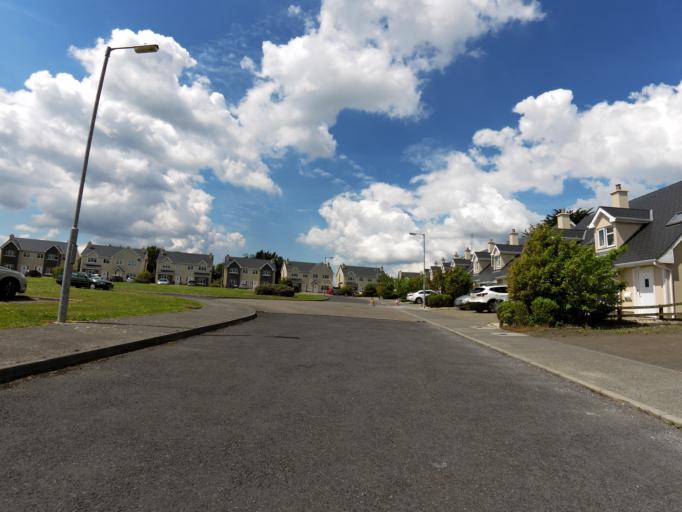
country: IE
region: Connaught
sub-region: County Galway
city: Athenry
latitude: 53.2953
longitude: -8.7537
